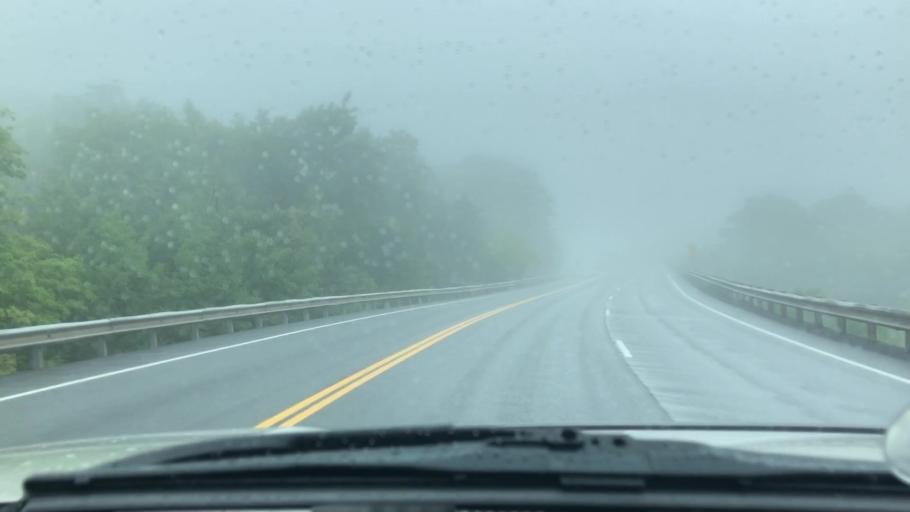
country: US
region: New York
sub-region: Greene County
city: Cairo
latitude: 42.3365
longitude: -74.1491
